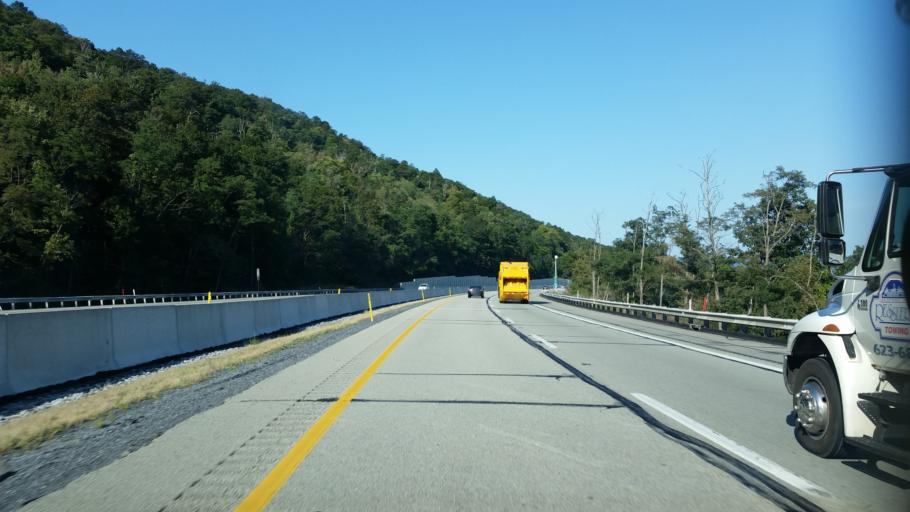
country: US
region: Pennsylvania
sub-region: Fulton County
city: McConnellsburg
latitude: 40.0479
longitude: -78.1192
